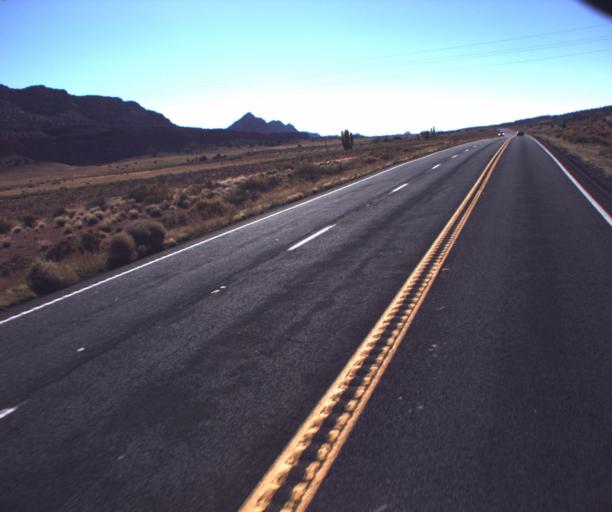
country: US
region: Arizona
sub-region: Coconino County
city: Tuba City
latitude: 36.4257
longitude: -111.5461
